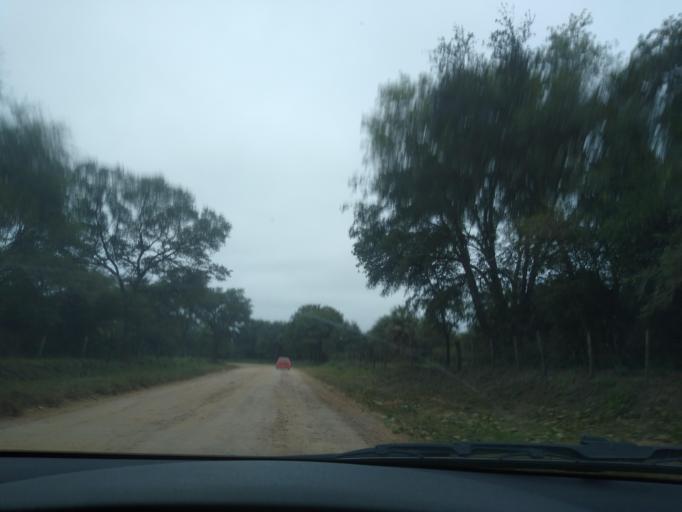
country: AR
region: Chaco
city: Colonia Benitez
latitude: -27.3428
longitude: -58.9693
